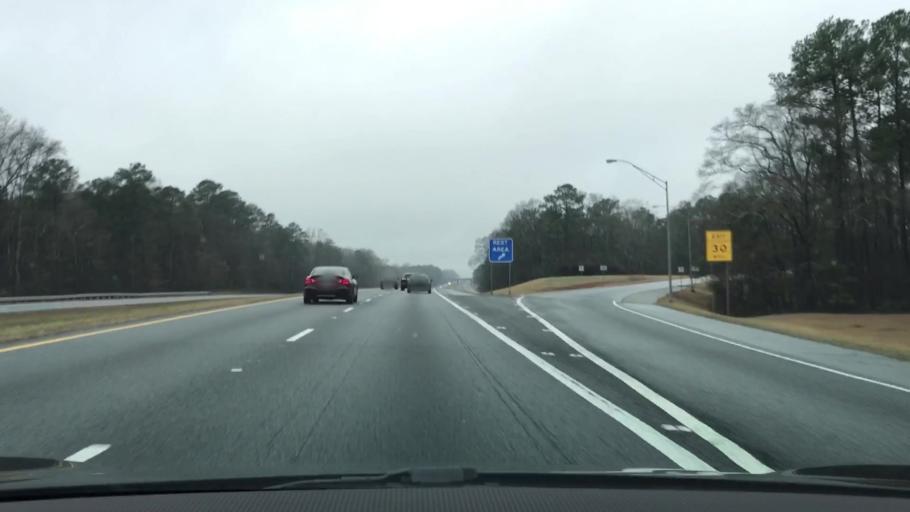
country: US
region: Georgia
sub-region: Morgan County
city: Madison
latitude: 33.5776
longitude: -83.5744
